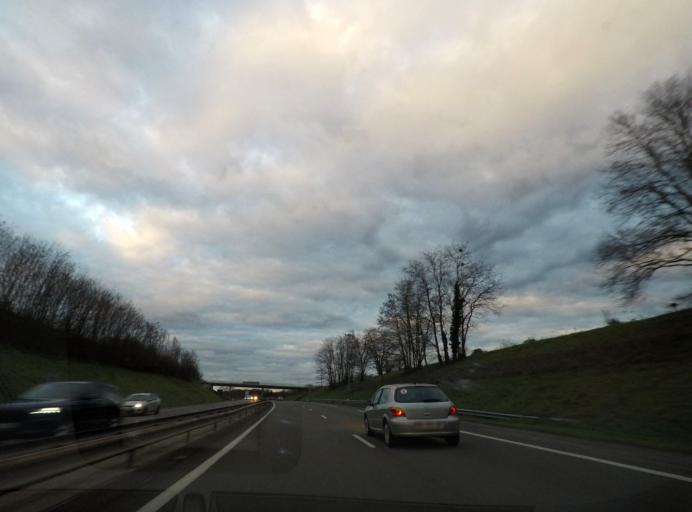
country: FR
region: Rhone-Alpes
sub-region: Departement de l'Ain
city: Neuville-sur-Ain
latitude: 46.0806
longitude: 5.3650
